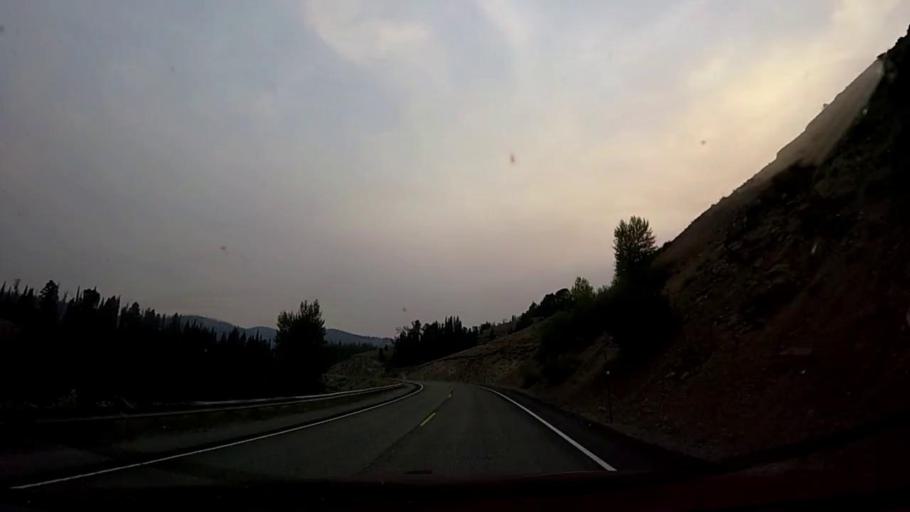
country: US
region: Idaho
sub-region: Blaine County
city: Ketchum
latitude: 43.8774
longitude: -114.7036
